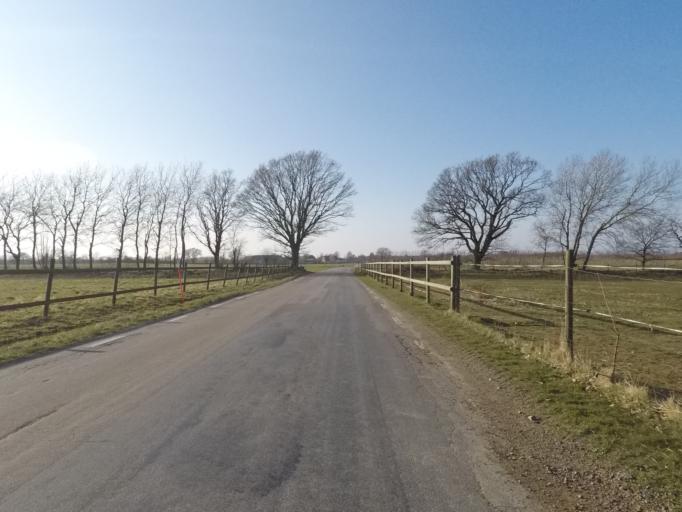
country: SE
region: Skane
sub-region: Hoganas Kommun
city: Hoganas
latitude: 56.2337
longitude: 12.6619
